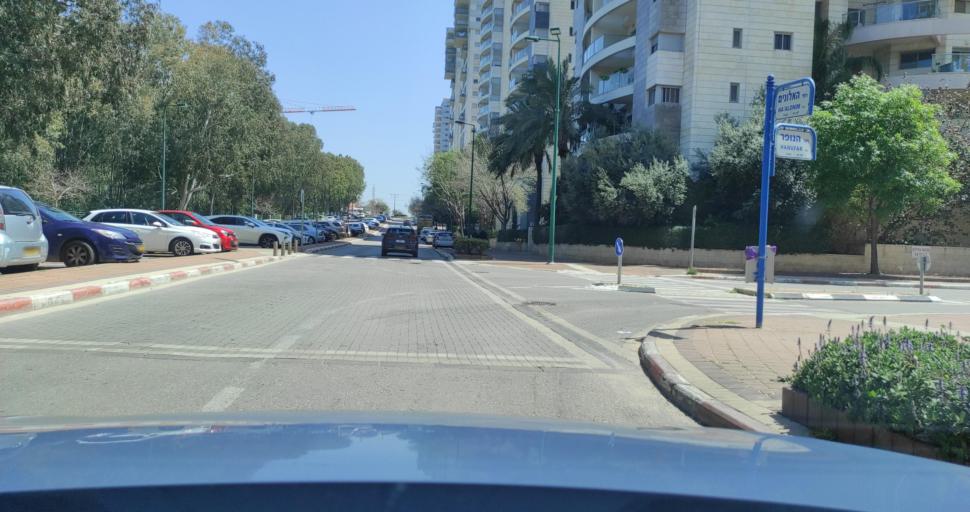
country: IL
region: Central District
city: Nordiyya
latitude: 32.3029
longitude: 34.8769
